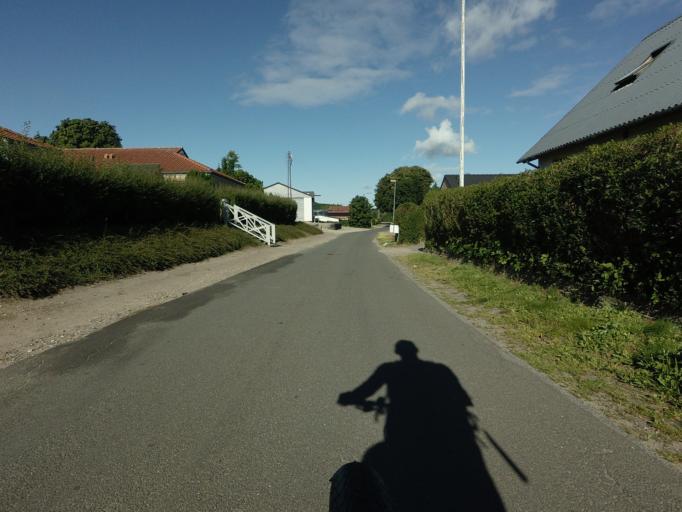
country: DK
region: Central Jutland
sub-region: Horsens Kommune
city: Horsens
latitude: 55.8960
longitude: 9.7701
